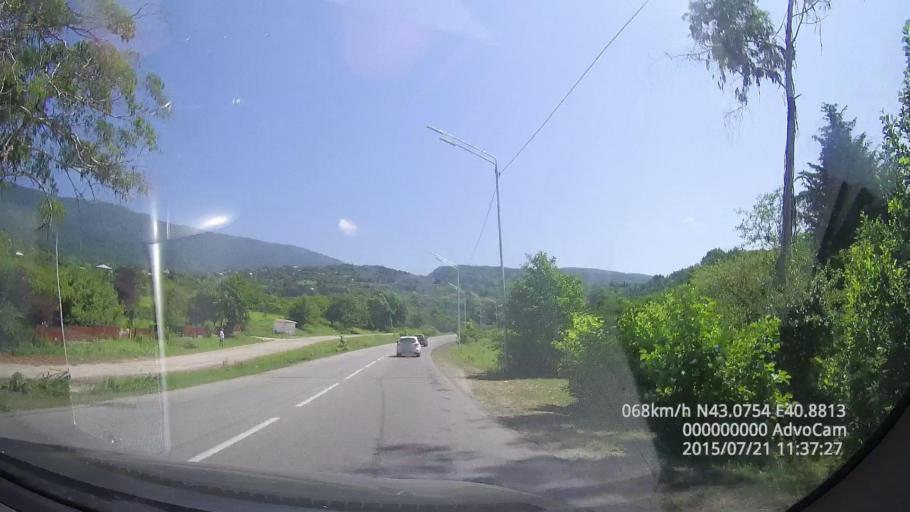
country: GE
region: Abkhazia
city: Stantsiya Novyy Afon
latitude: 43.0757
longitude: 40.8819
